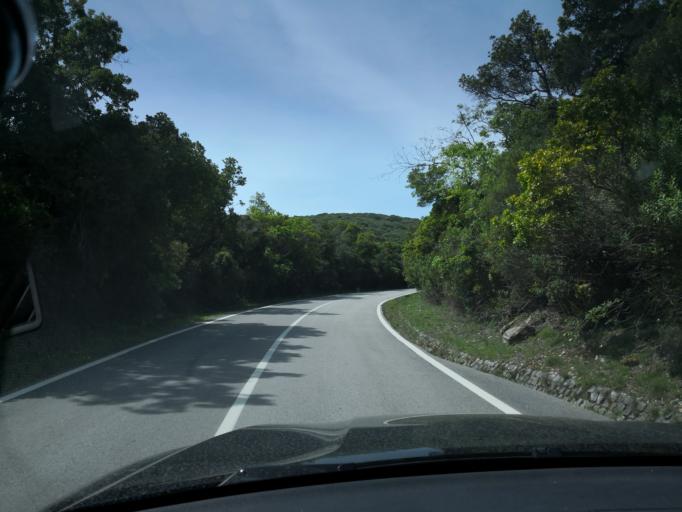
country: PT
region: Setubal
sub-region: Sesimbra
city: Sesimbra
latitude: 38.4633
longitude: -9.0012
